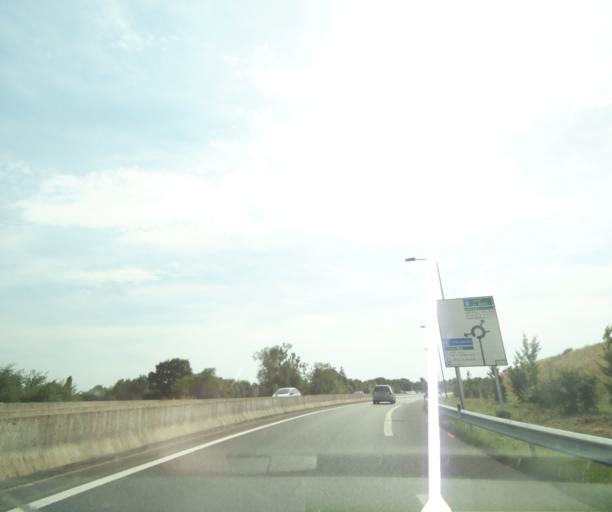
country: FR
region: Centre
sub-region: Departement d'Indre-et-Loire
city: Mettray
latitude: 47.4305
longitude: 0.6533
